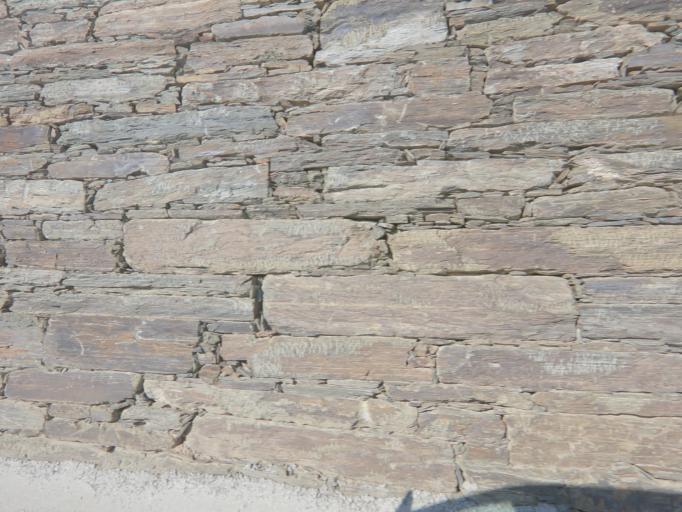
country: PT
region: Vila Real
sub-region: Sabrosa
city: Vilela
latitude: 41.1753
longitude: -7.5782
